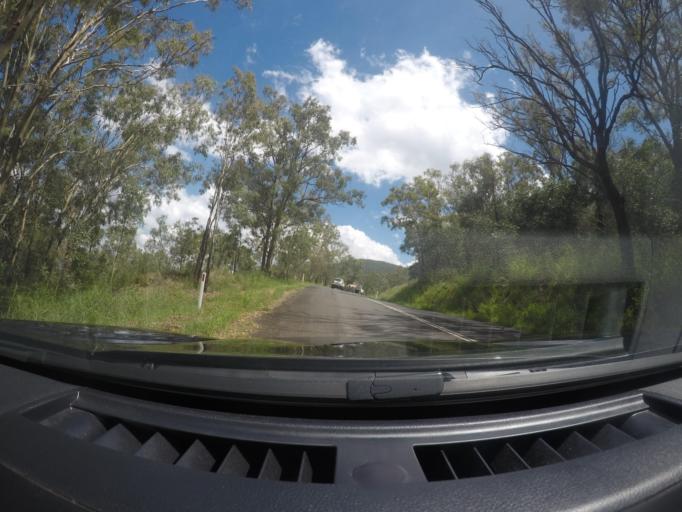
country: AU
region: Queensland
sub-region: Moreton Bay
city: Woodford
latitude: -27.1049
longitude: 152.5603
